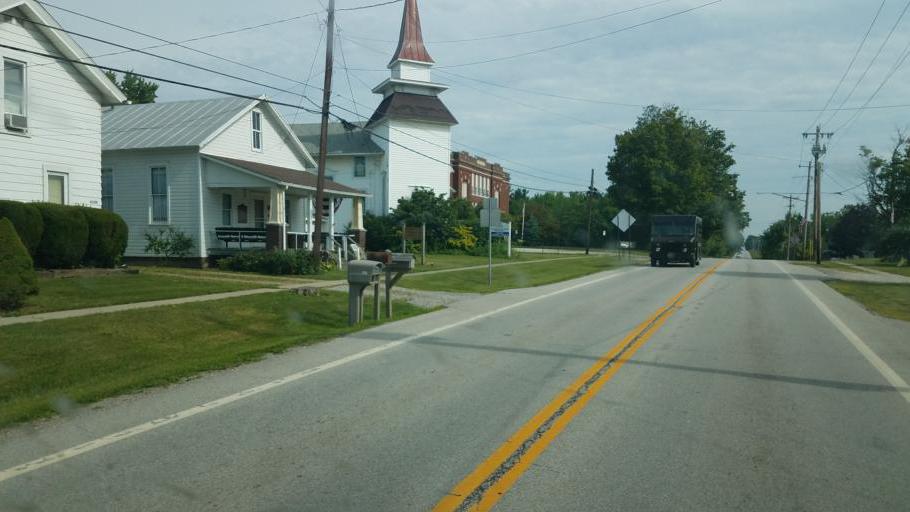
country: US
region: Ohio
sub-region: Medina County
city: Lodi
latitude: 41.1009
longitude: -82.0243
